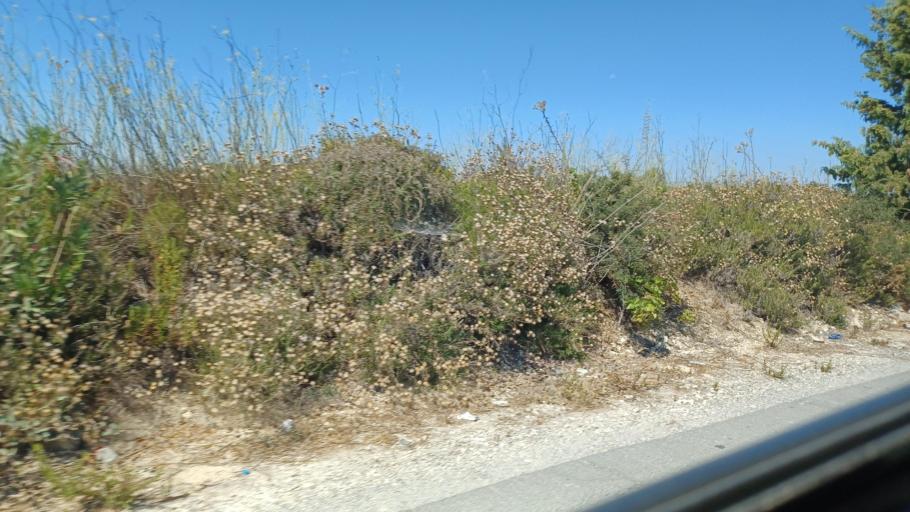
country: CY
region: Pafos
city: Mesogi
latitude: 34.8344
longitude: 32.4897
